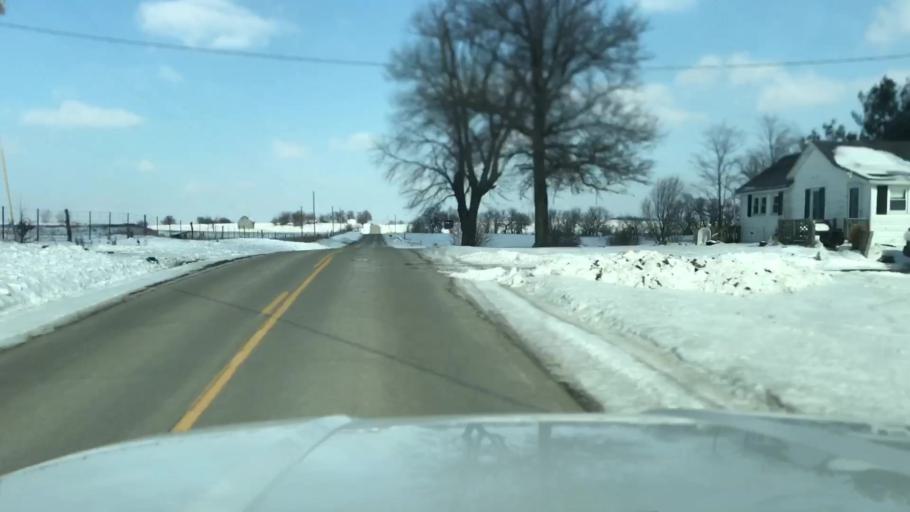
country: US
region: Missouri
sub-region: Nodaway County
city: Maryville
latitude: 40.3478
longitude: -94.7224
